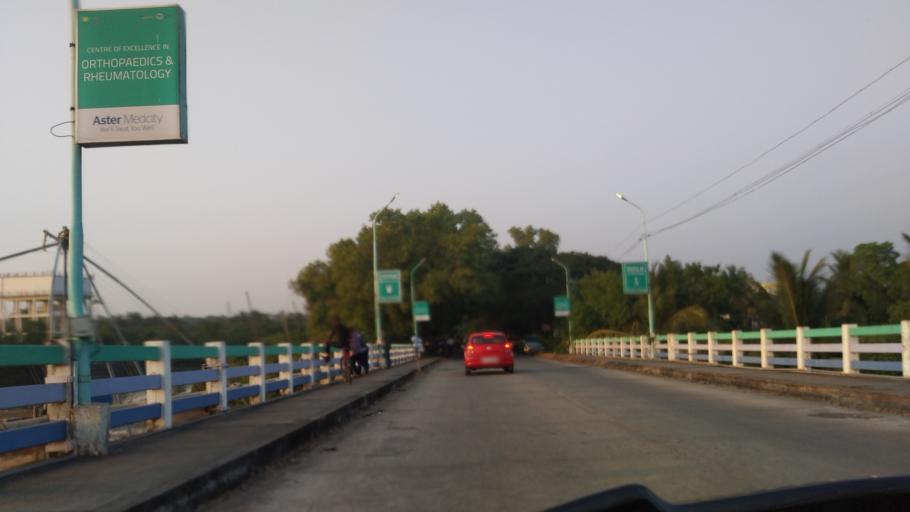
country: IN
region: Kerala
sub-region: Ernakulam
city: Elur
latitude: 10.0473
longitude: 76.2732
